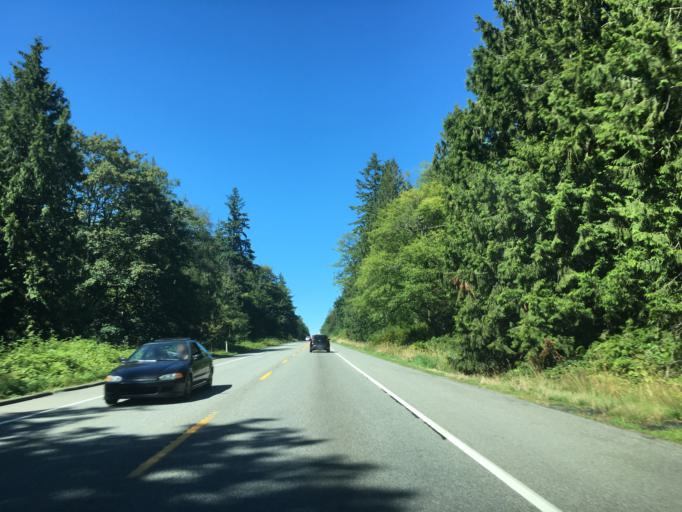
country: US
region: Washington
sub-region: Snohomish County
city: Sisco Heights
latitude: 48.0824
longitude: -122.1116
